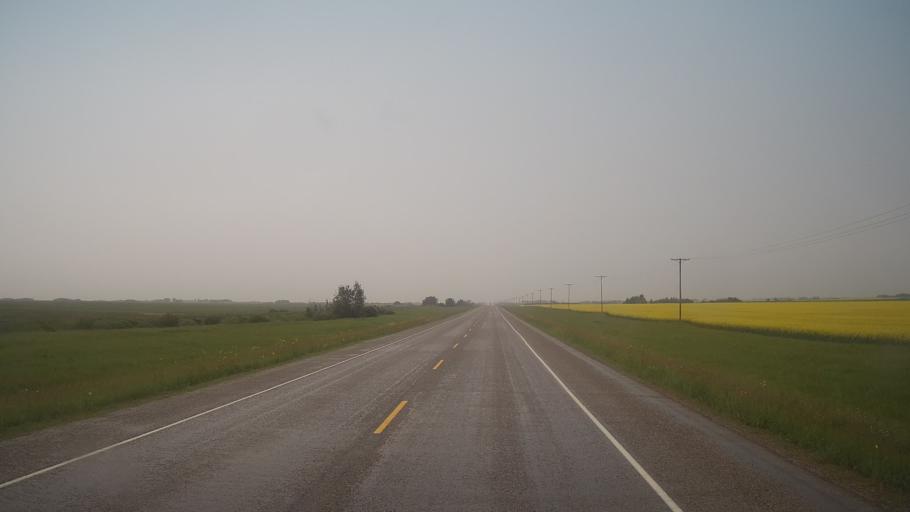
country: CA
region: Saskatchewan
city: Biggar
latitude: 52.1486
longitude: -108.2219
